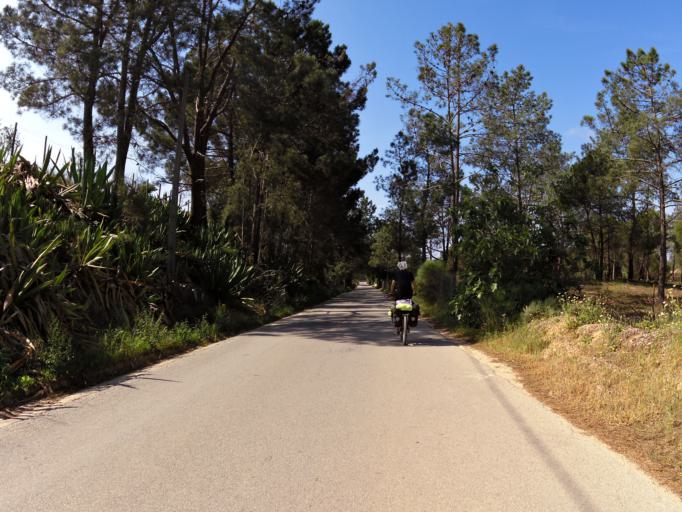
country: PT
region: Faro
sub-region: Loule
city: Almancil
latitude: 37.0636
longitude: -8.0154
